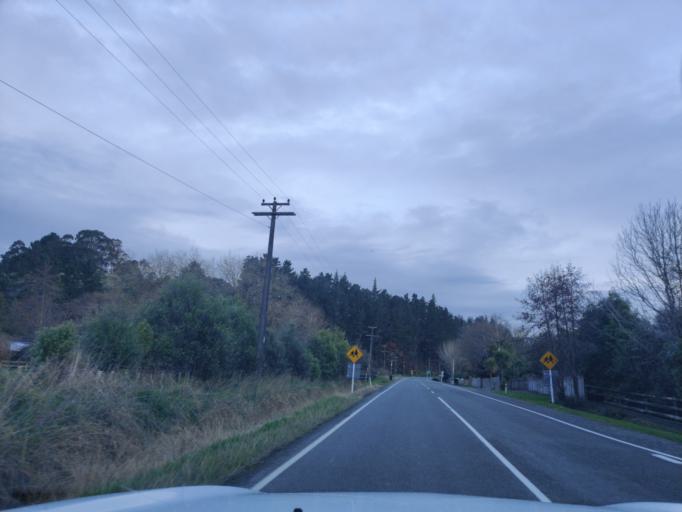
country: NZ
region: Manawatu-Wanganui
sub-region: Palmerston North City
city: Palmerston North
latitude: -40.3656
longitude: 175.6639
